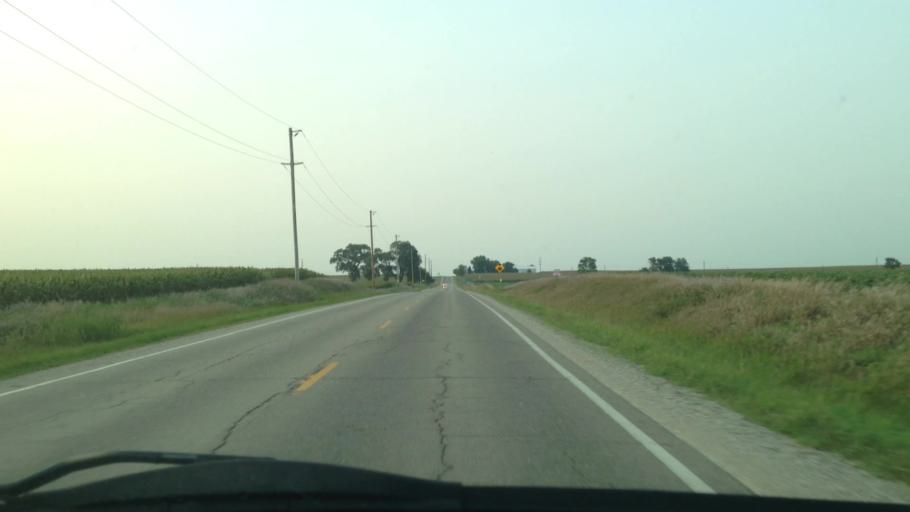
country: US
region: Iowa
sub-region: Iowa County
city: Marengo
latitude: 41.9587
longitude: -92.0853
